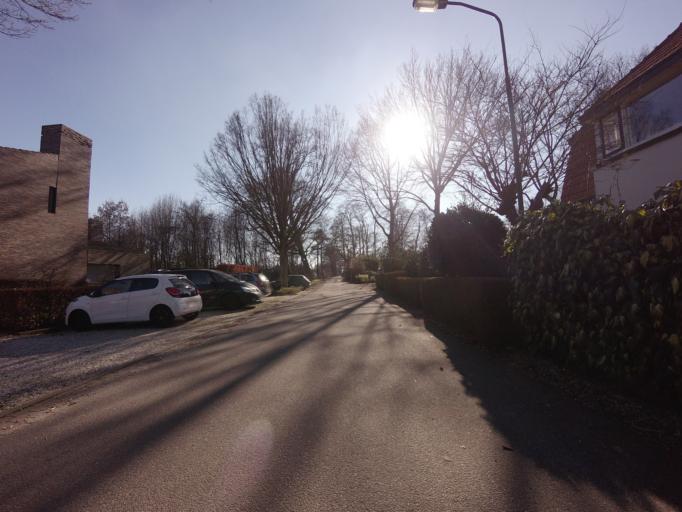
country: NL
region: Utrecht
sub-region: Gemeente De Bilt
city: De Bilt
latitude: 52.1243
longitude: 5.1591
